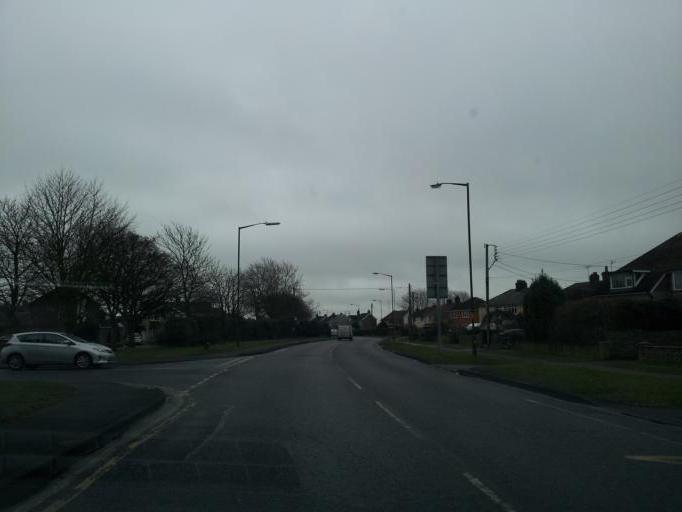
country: GB
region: England
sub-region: Essex
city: Manningtree
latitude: 51.9383
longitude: 1.0473
